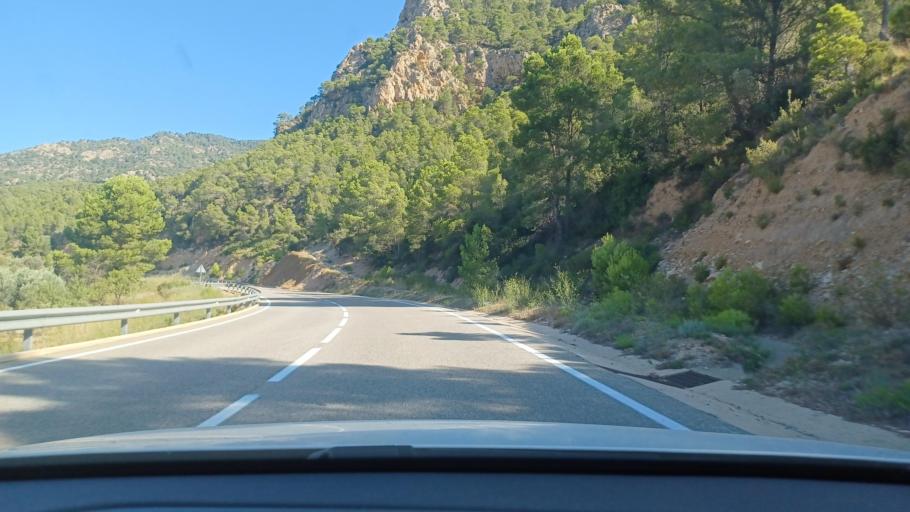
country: ES
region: Catalonia
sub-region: Provincia de Tarragona
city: Bot
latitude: 40.9720
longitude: 0.4294
